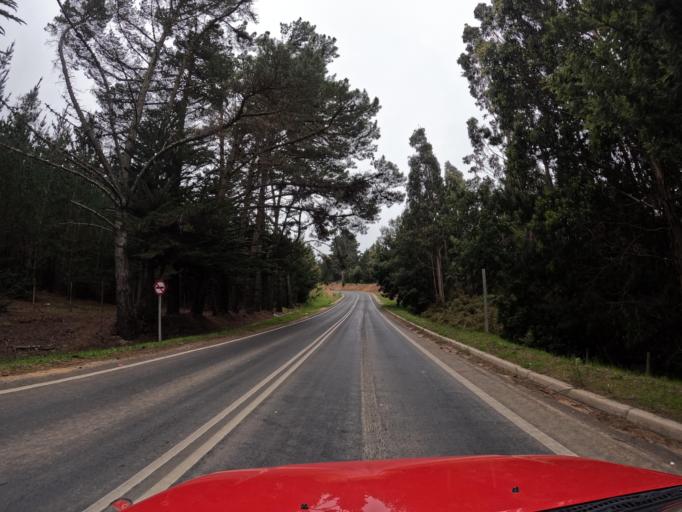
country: CL
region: O'Higgins
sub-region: Provincia de Colchagua
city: Santa Cruz
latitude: -34.5884
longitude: -72.0147
